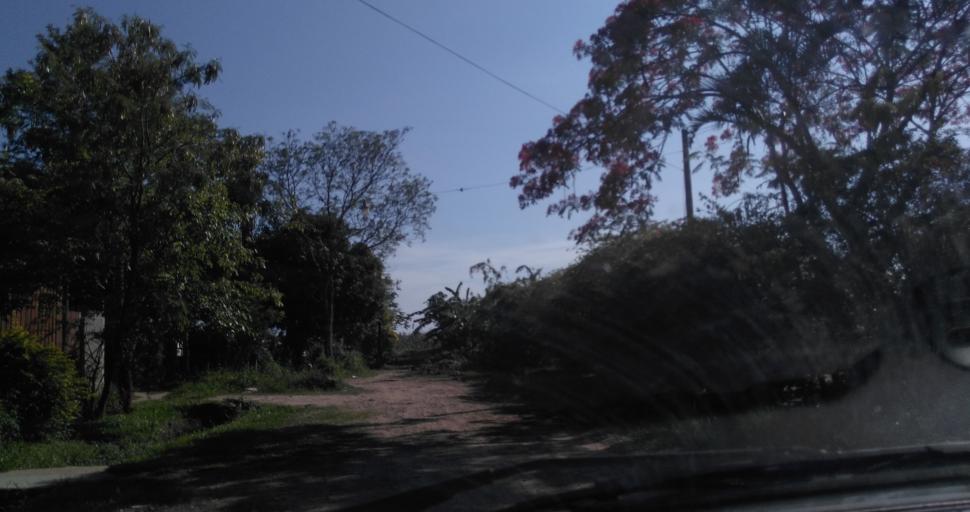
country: AR
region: Chaco
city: Resistencia
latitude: -27.4628
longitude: -58.9653
